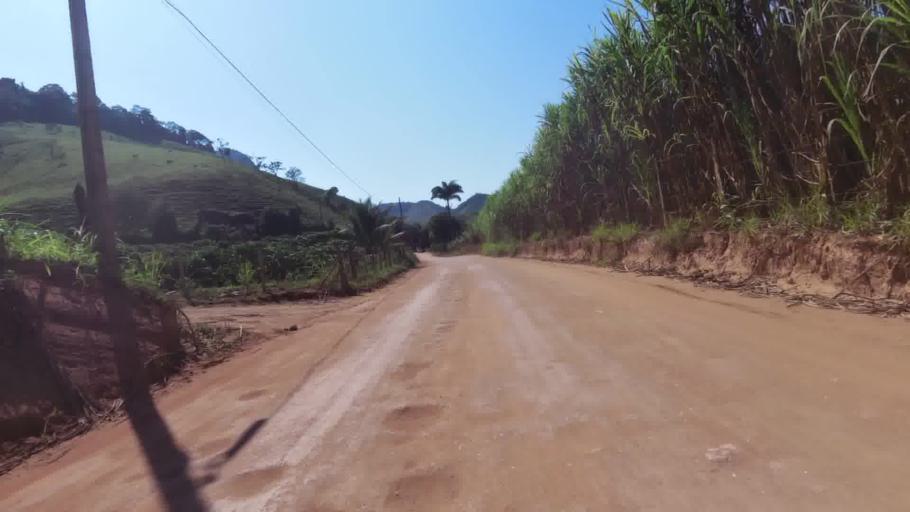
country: BR
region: Espirito Santo
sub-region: Alfredo Chaves
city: Alfredo Chaves
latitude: -20.6377
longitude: -40.7715
